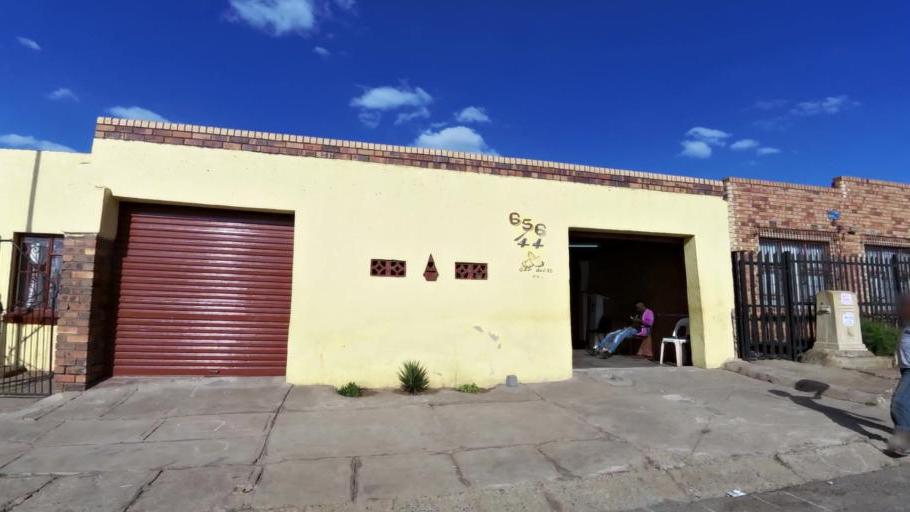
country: ZA
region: Gauteng
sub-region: City of Johannesburg Metropolitan Municipality
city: Soweto
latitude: -26.2270
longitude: 27.8771
